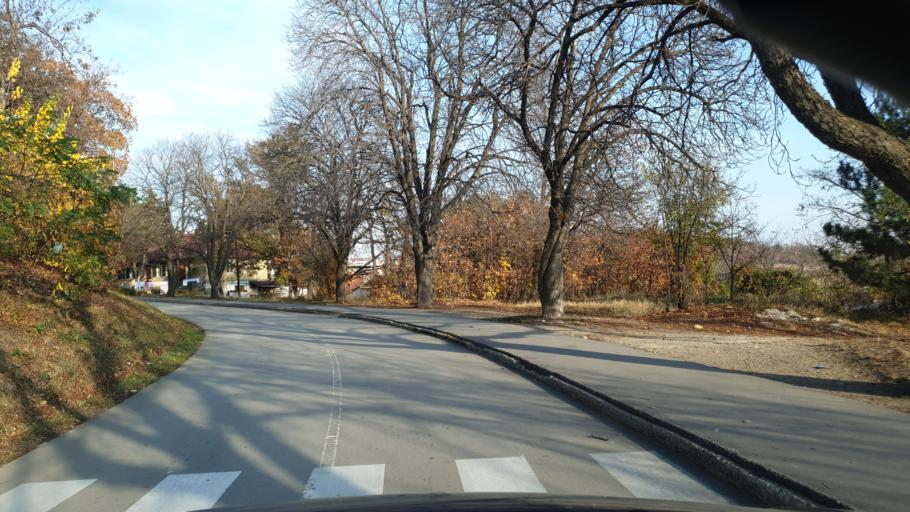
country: RS
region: Central Serbia
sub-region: Borski Okrug
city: Bor
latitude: 44.0518
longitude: 22.0978
